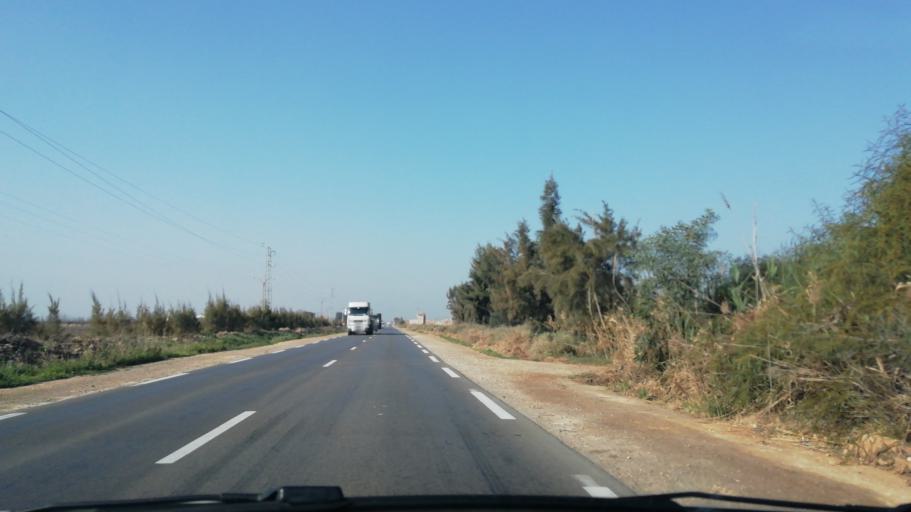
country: DZ
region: Mostaganem
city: Mostaganem
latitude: 35.7461
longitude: 0.0201
